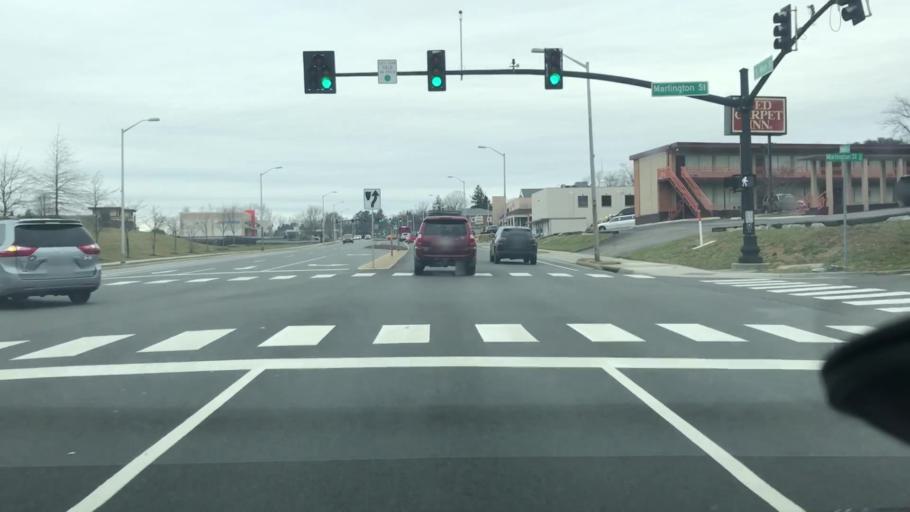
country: US
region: Virginia
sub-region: Montgomery County
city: Blacksburg
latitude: 37.2114
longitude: -80.3996
